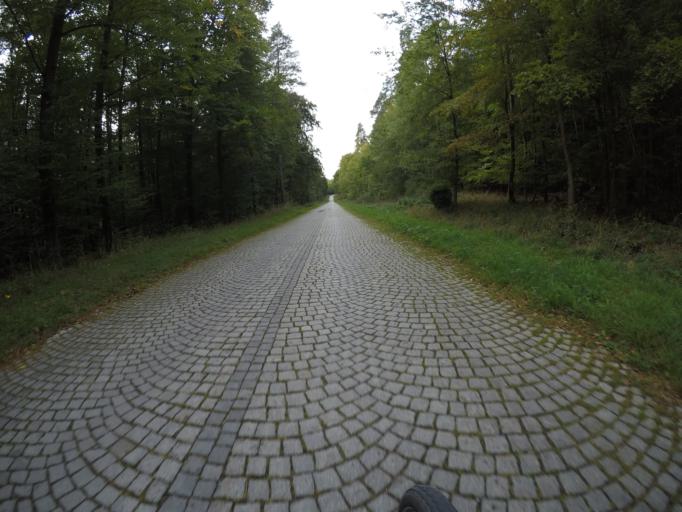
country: DE
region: Baden-Wuerttemberg
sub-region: Regierungsbezirk Stuttgart
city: Steinenbronn
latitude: 48.7127
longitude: 9.0826
